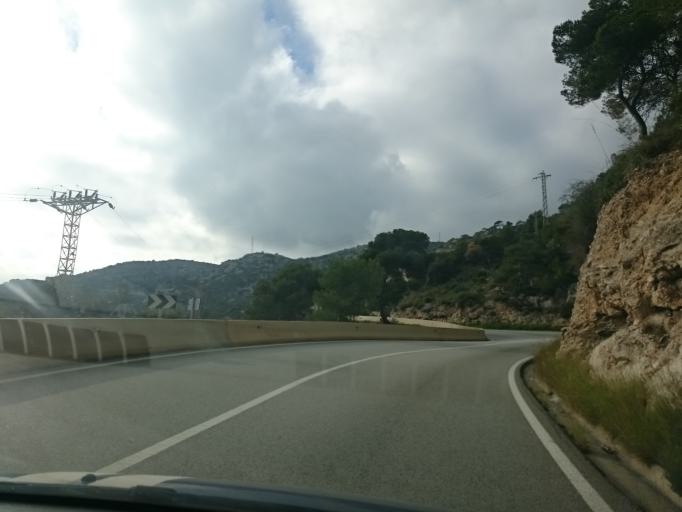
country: ES
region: Catalonia
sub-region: Provincia de Barcelona
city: Castelldefels
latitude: 41.2533
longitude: 1.8973
